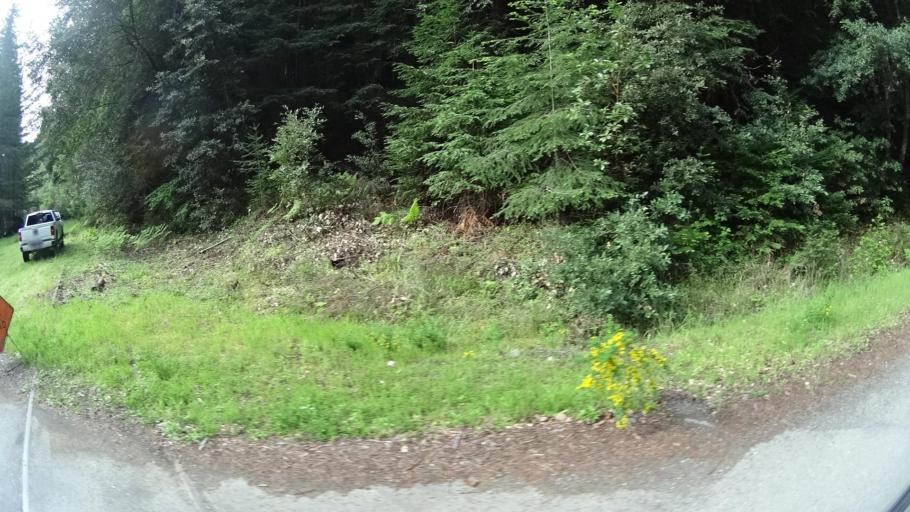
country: US
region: California
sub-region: Humboldt County
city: Redway
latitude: 40.3282
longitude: -123.8427
